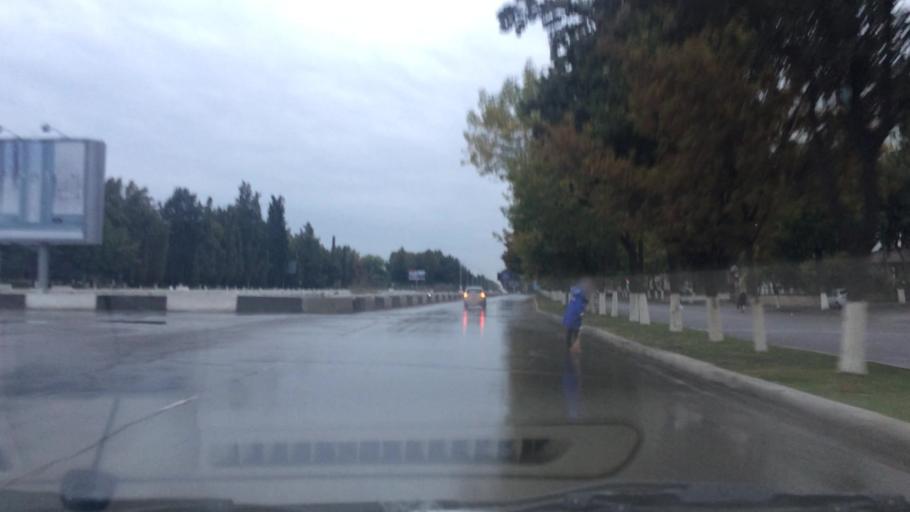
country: UZ
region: Toshkent Shahri
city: Tashkent
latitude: 41.3106
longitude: 69.2401
